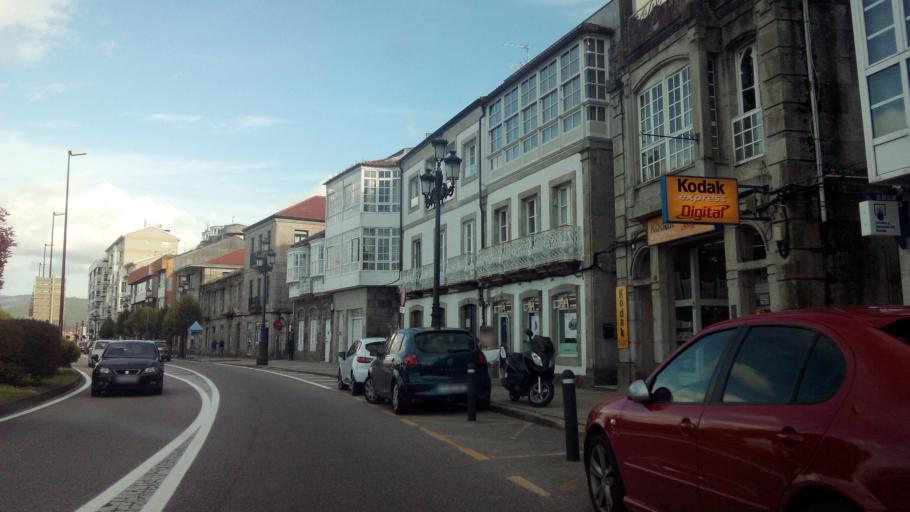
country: ES
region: Galicia
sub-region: Provincia de Pontevedra
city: Baiona
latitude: 42.1185
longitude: -8.8471
